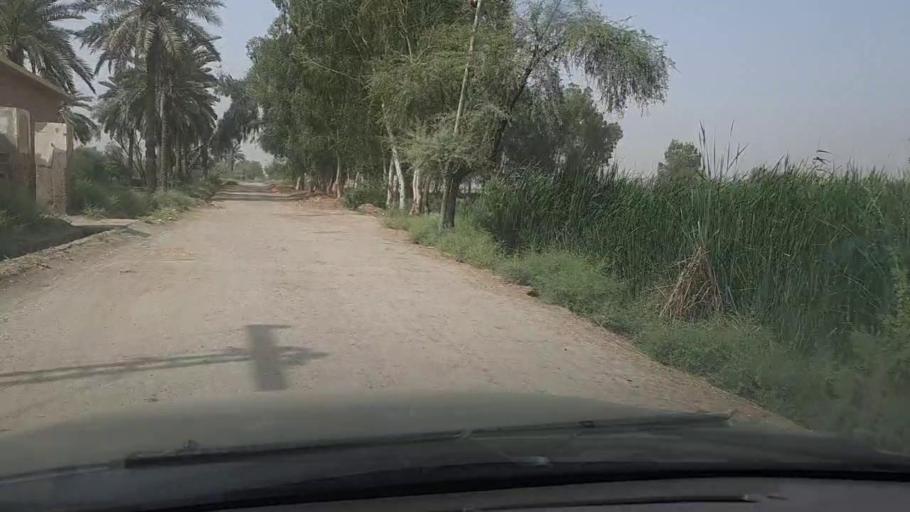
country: PK
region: Sindh
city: Garhi Yasin
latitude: 27.8614
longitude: 68.5493
